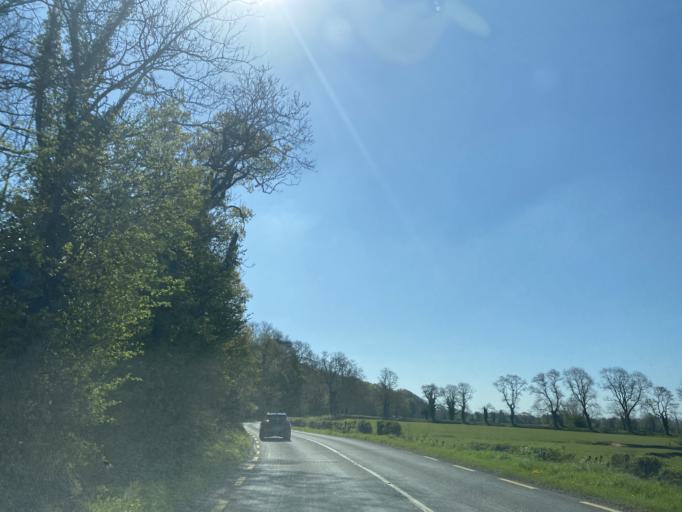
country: IE
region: Leinster
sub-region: Kildare
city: Kill
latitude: 53.2626
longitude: -6.5870
